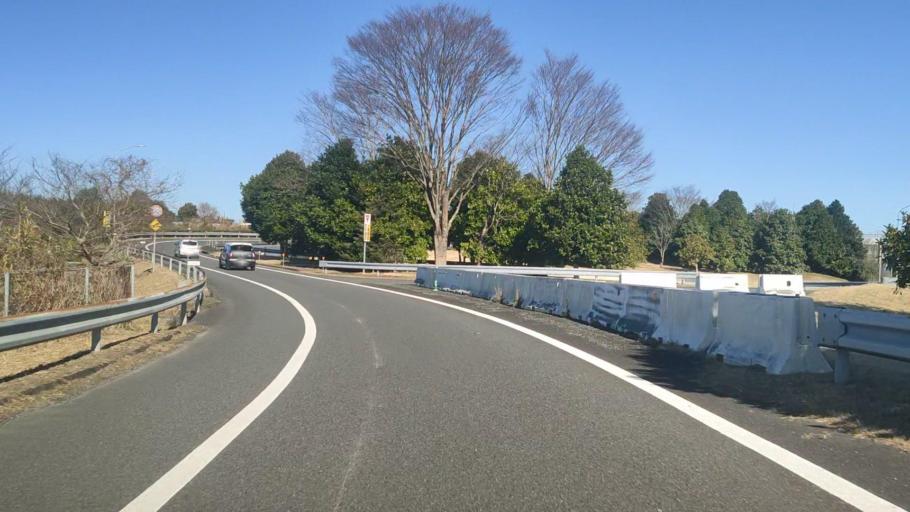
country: JP
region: Miyazaki
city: Miyakonojo
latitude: 31.7811
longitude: 131.1098
